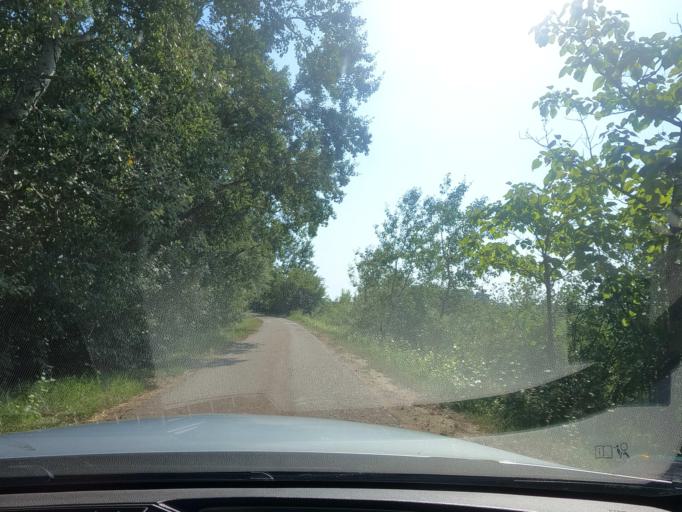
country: RS
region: Autonomna Pokrajina Vojvodina
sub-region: Juznobacki Okrug
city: Becej
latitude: 45.6578
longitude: 19.9017
